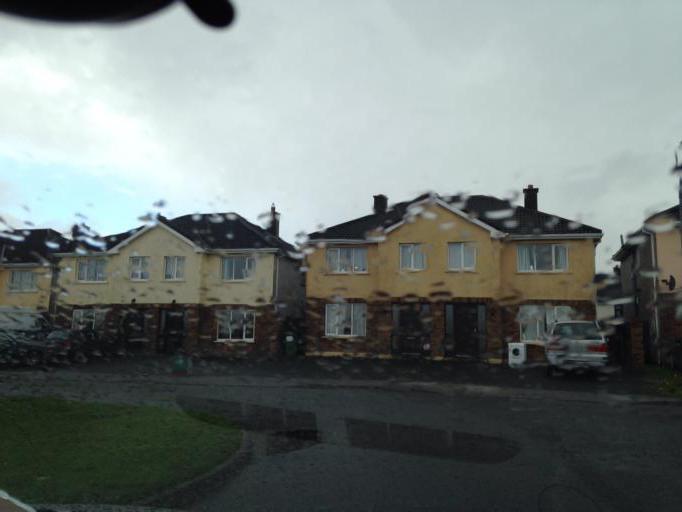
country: IE
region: Connaught
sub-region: County Galway
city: Gaillimh
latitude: 53.2724
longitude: -9.0072
